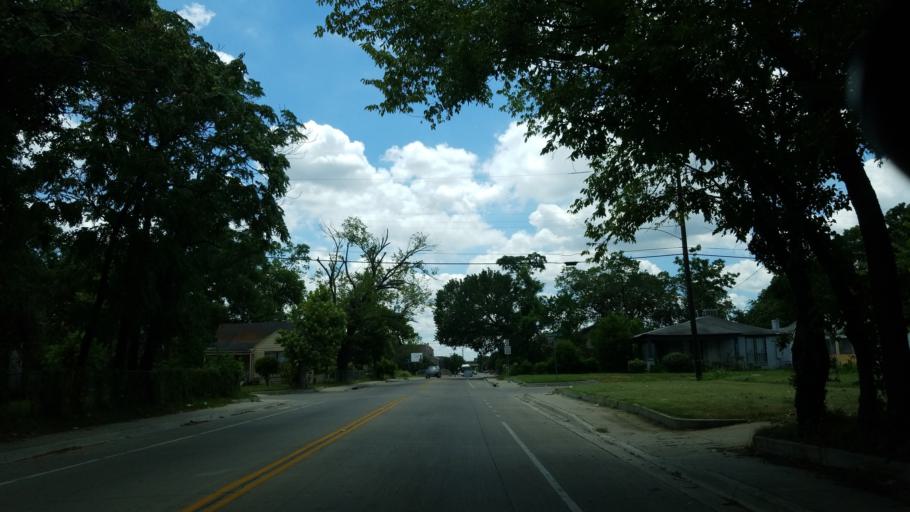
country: US
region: Texas
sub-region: Dallas County
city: Dallas
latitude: 32.7525
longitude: -96.7533
